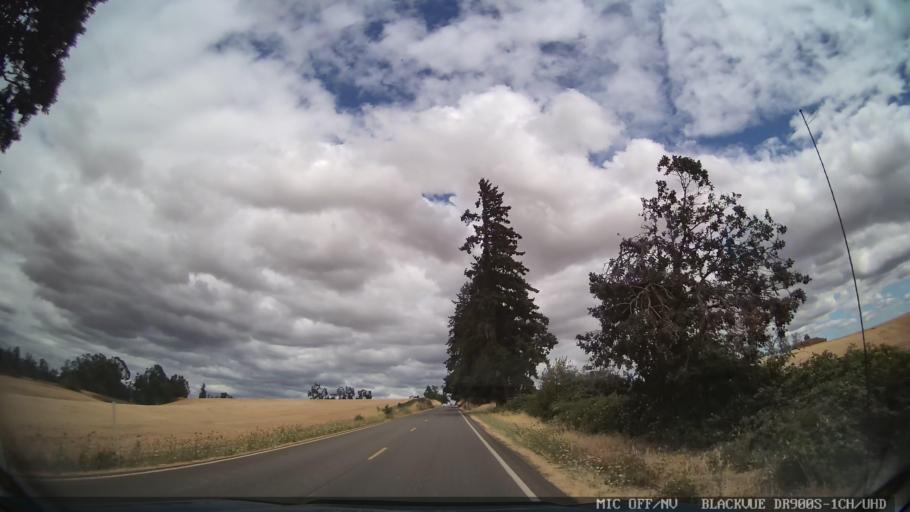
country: US
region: Oregon
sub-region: Marion County
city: Sublimity
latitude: 44.8655
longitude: -122.8207
